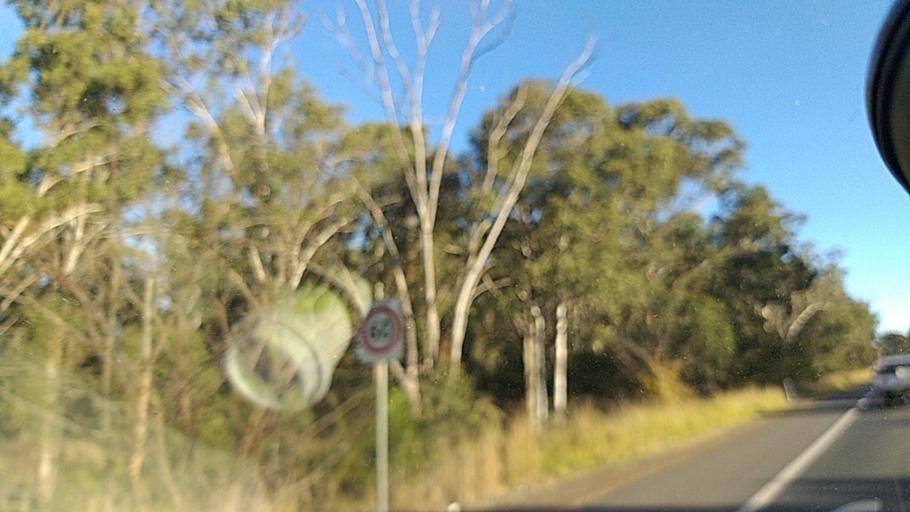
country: AU
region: New South Wales
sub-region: Hawkesbury
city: South Windsor
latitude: -33.6321
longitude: 150.7911
